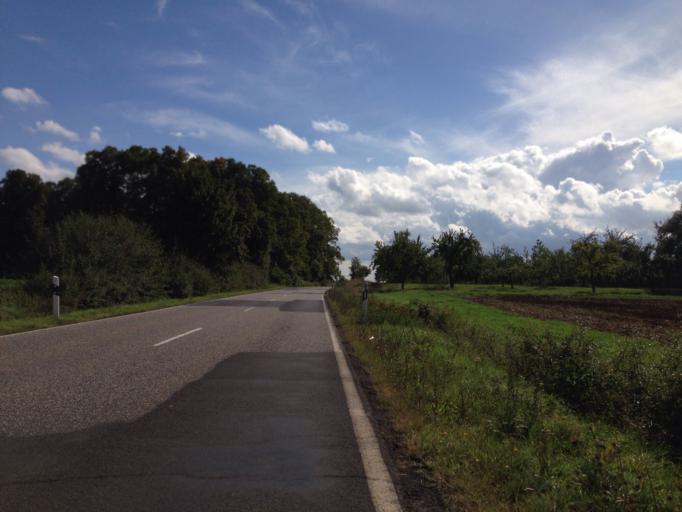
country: DE
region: Hesse
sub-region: Regierungsbezirk Giessen
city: Hungen
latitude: 50.4863
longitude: 8.9019
